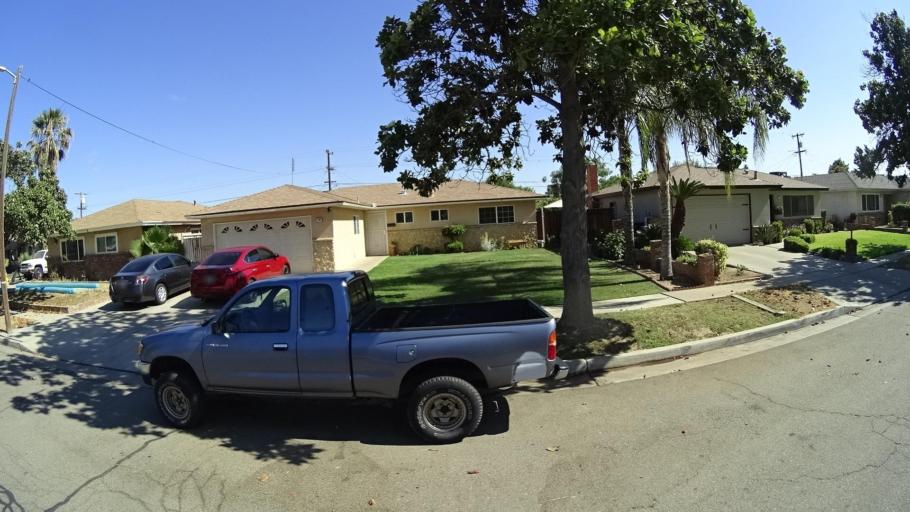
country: US
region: California
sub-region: Fresno County
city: West Park
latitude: 36.7784
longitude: -119.8381
